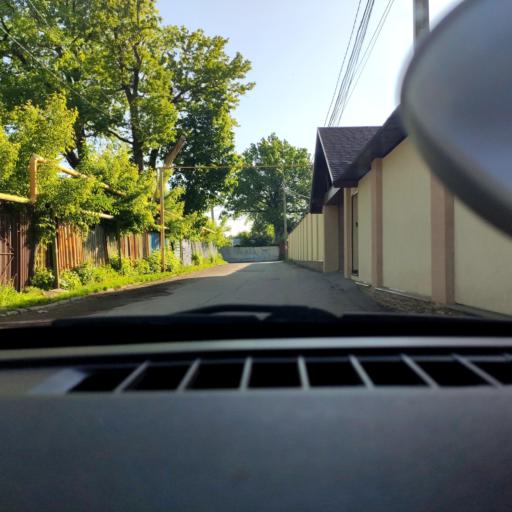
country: RU
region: Samara
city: Samara
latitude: 53.2722
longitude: 50.1876
